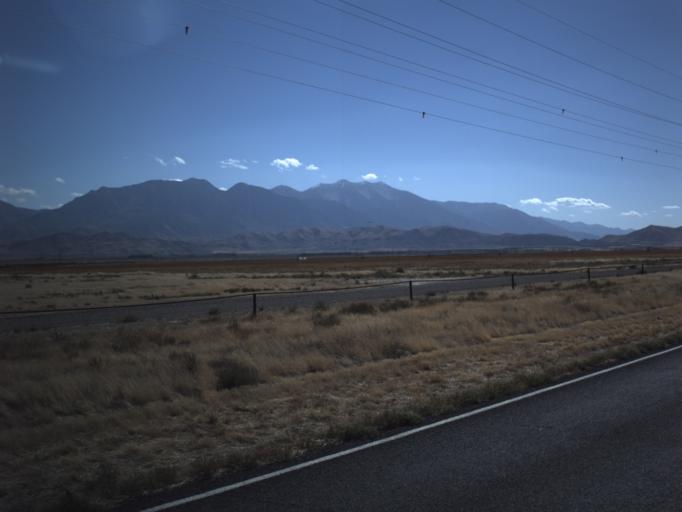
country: US
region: Utah
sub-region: Utah County
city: Genola
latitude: 40.0254
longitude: -111.9583
